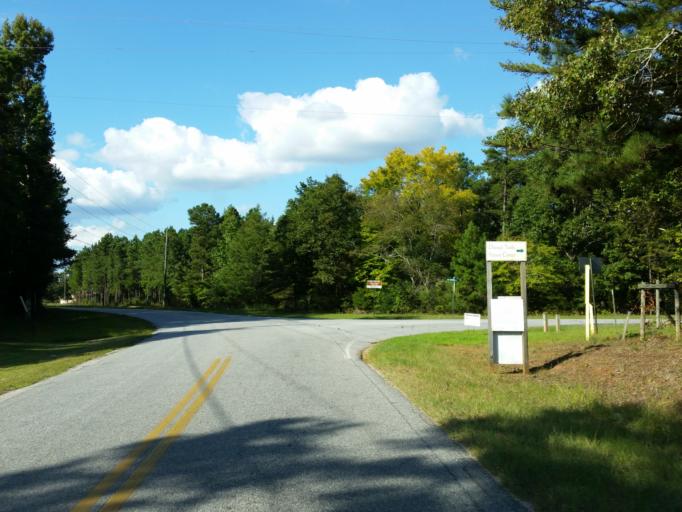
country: US
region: Georgia
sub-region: Butts County
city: Indian Springs
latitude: 33.2150
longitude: -83.9957
